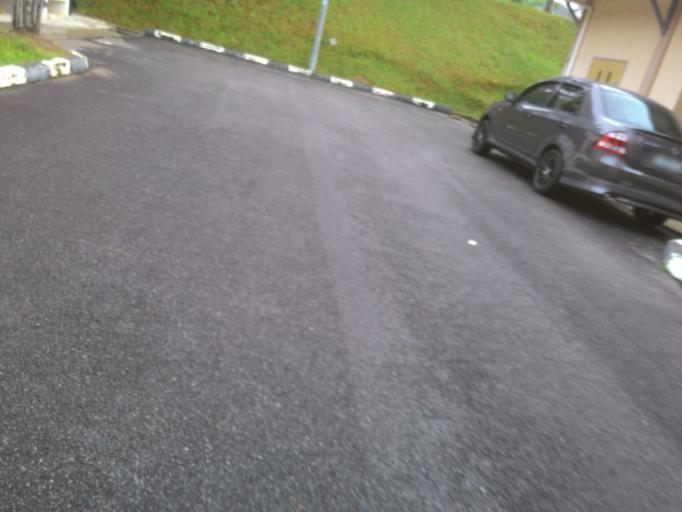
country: MY
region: Kedah
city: Kulim
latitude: 5.3839
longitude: 100.5799
